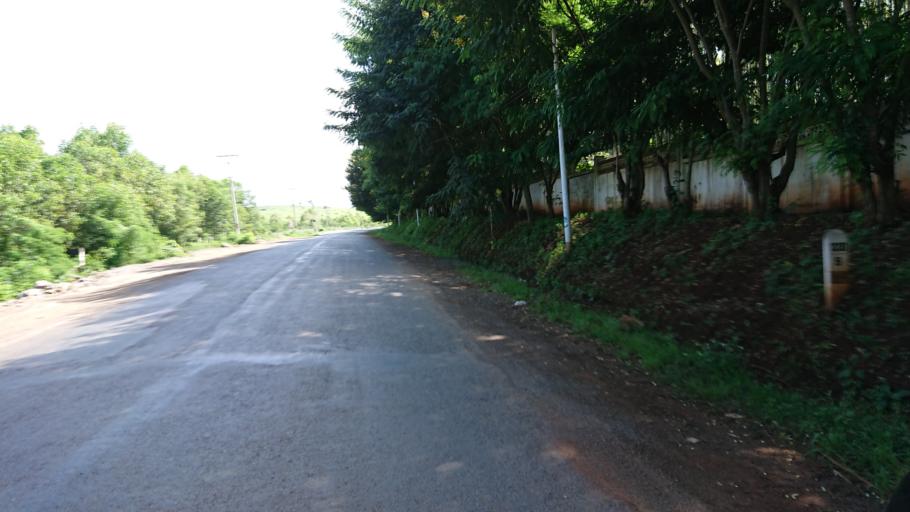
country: MM
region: Shan
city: Taunggyi
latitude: 20.8037
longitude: 97.1861
